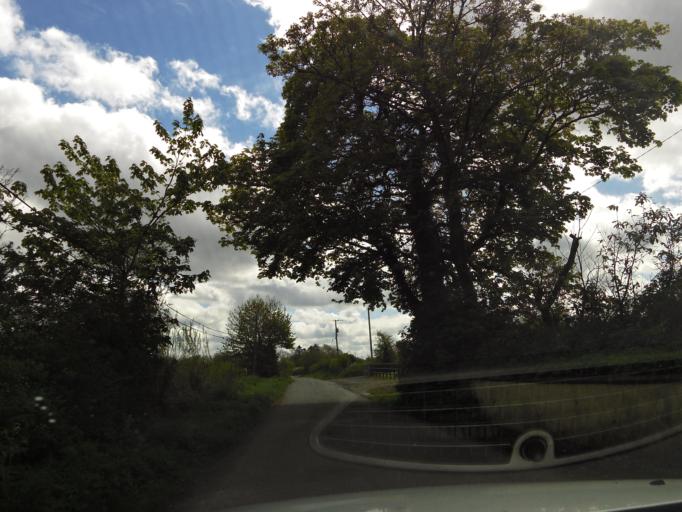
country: IE
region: Connaught
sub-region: Maigh Eo
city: Kiltamagh
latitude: 53.8003
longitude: -8.9704
